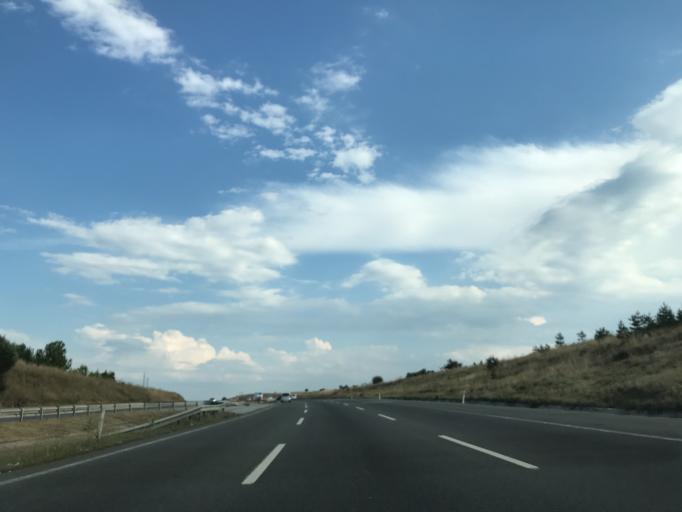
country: TR
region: Bolu
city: Yenicaga
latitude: 40.7591
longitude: 32.0629
